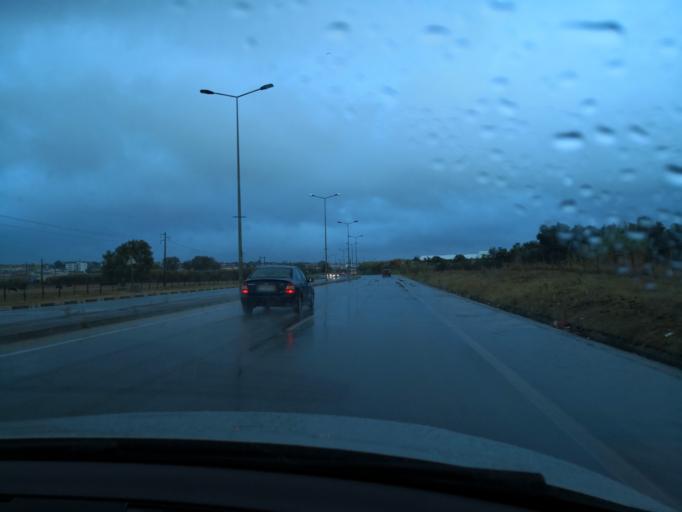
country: PT
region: Setubal
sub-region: Moita
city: Moita
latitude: 38.6512
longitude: -9.0035
